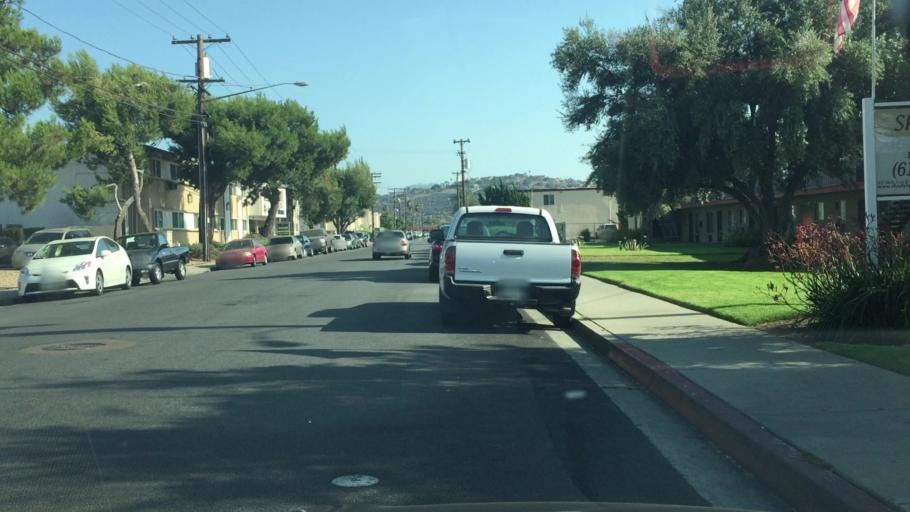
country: US
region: California
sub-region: San Diego County
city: Bostonia
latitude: 32.7994
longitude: -116.9380
